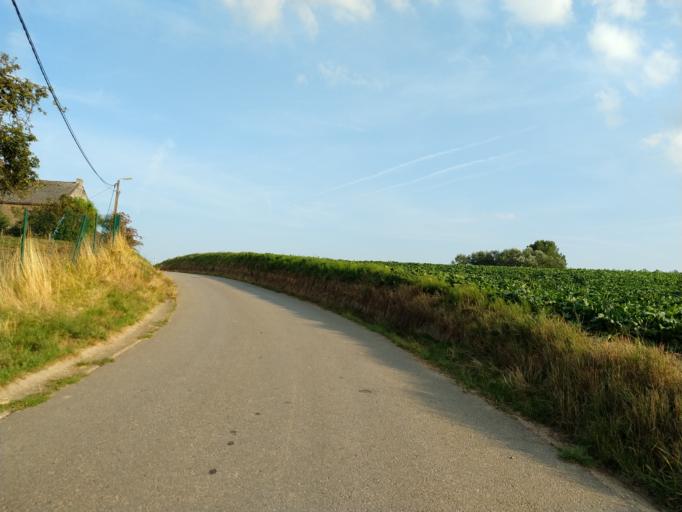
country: BE
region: Flanders
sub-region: Provincie Vlaams-Brabant
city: Boutersem
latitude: 50.8083
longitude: 4.8410
